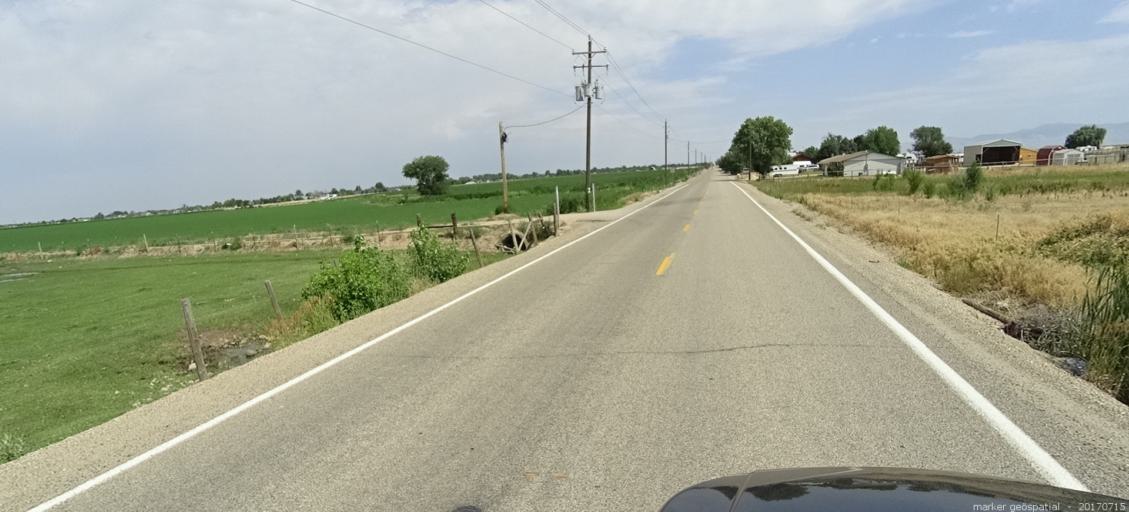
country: US
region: Idaho
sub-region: Ada County
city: Garden City
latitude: 43.5317
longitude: -116.2742
